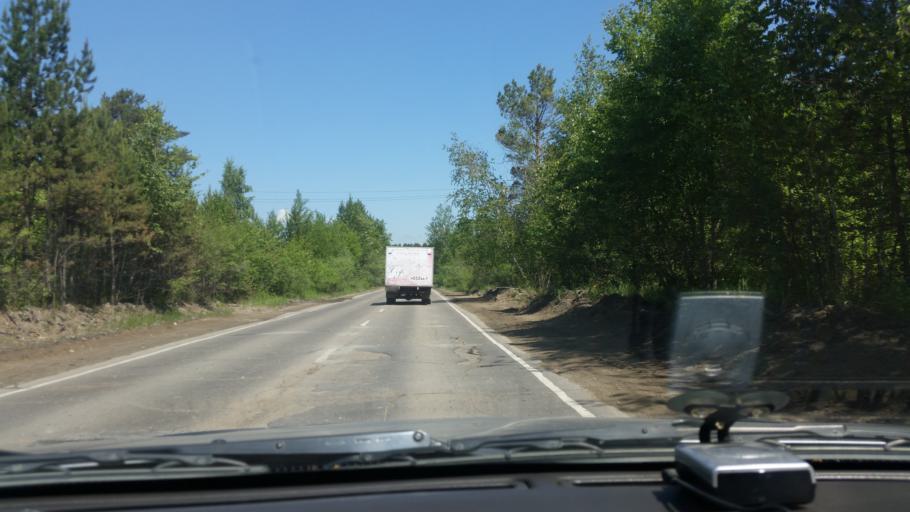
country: RU
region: Irkutsk
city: Shelekhov
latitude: 52.1925
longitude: 104.1119
